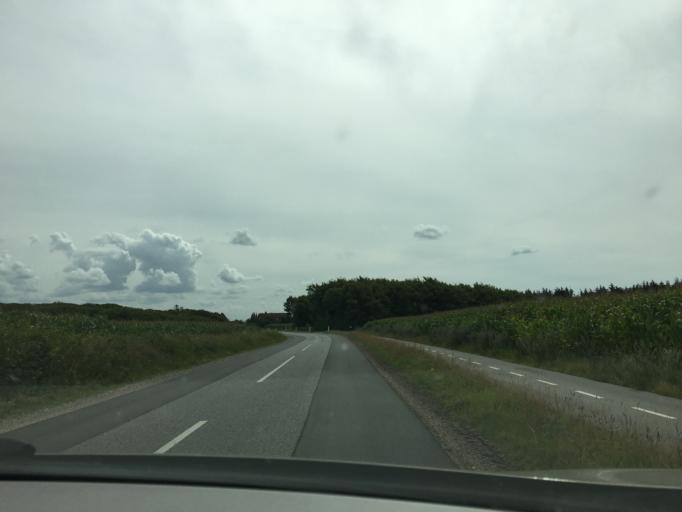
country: DK
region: Central Jutland
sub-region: Ringkobing-Skjern Kommune
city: Skjern
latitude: 55.9746
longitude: 8.3562
